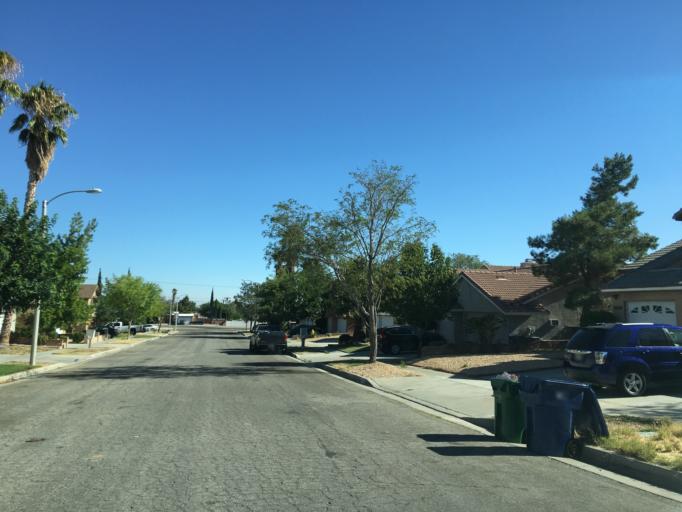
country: US
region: California
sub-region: Los Angeles County
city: Desert View Highlands
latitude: 34.5854
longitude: -118.1534
